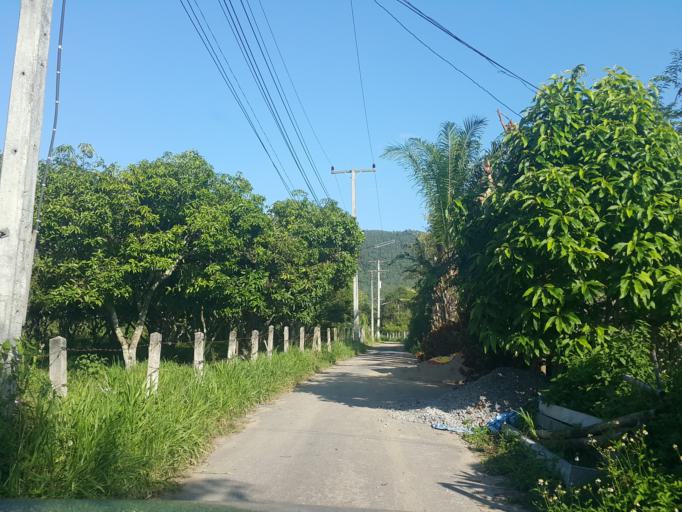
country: TH
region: Chiang Mai
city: Mae On
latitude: 18.7157
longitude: 99.2091
